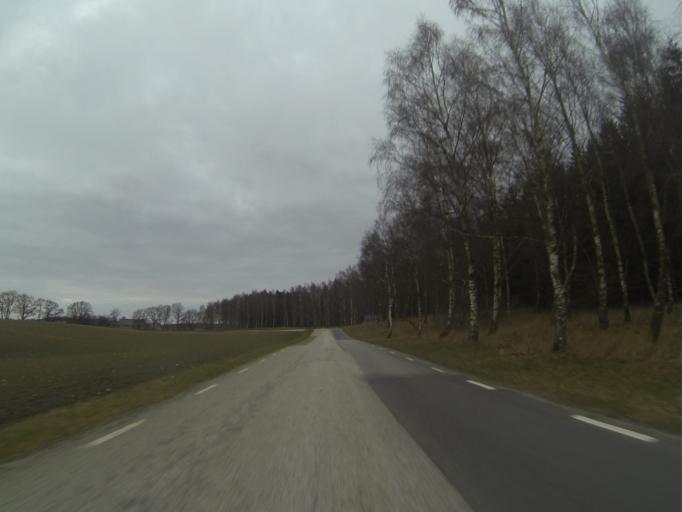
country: SE
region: Skane
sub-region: Skurups Kommun
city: Skurup
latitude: 55.5304
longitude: 13.4408
